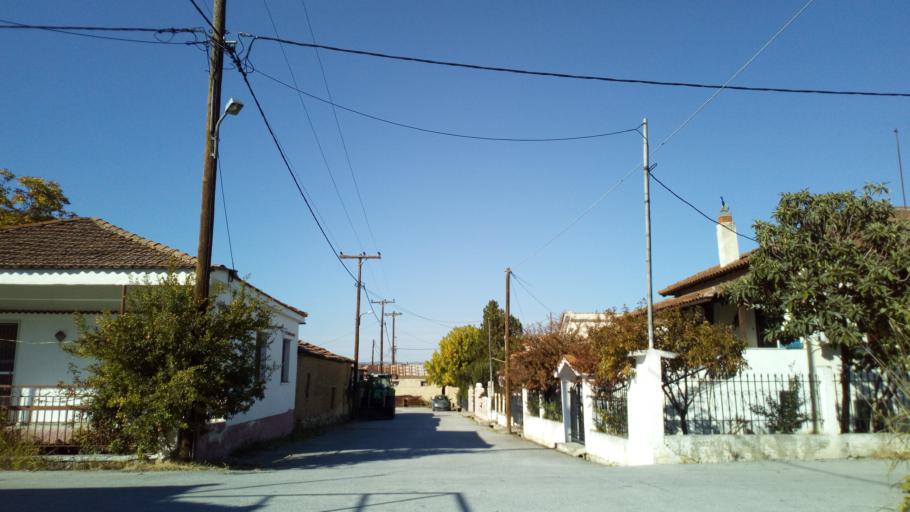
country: GR
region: Central Macedonia
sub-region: Nomos Thessalonikis
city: Gerakarou
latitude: 40.6348
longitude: 23.2492
